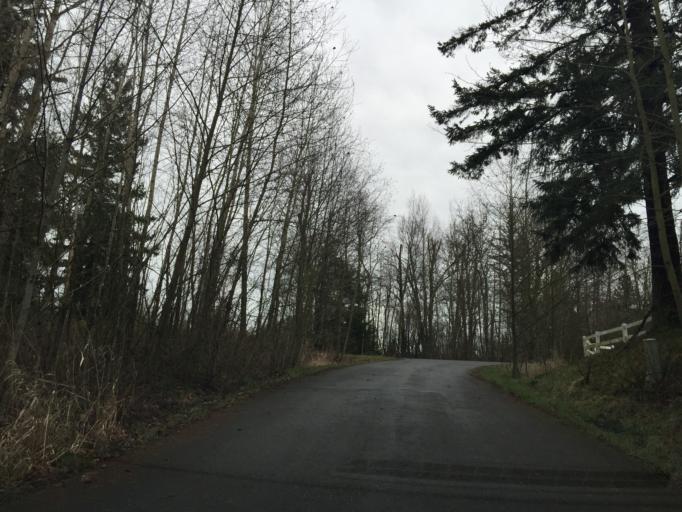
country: US
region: Washington
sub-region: Whatcom County
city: Geneva
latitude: 48.8064
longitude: -122.4323
